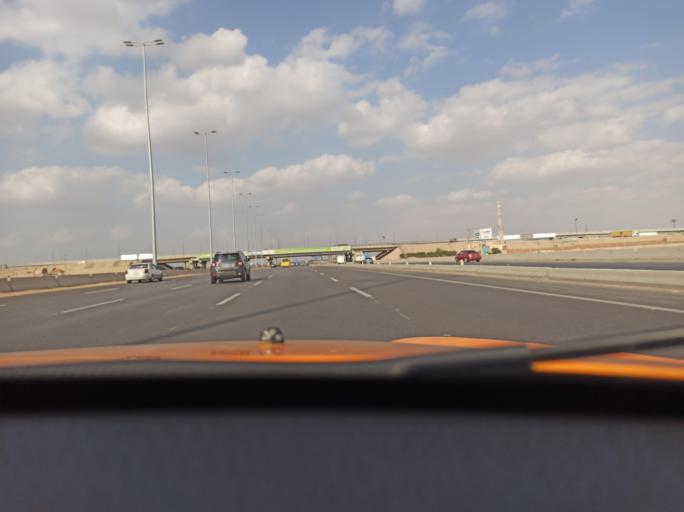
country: EG
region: Eastern Province
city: Bilbays
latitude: 30.2221
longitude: 31.6931
